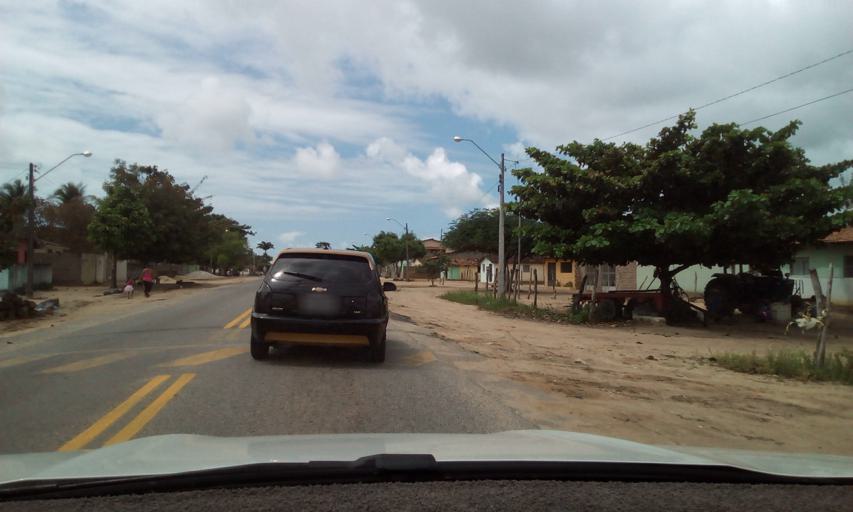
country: BR
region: Paraiba
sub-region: Rio Tinto
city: Rio Tinto
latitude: -6.7700
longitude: -35.0195
